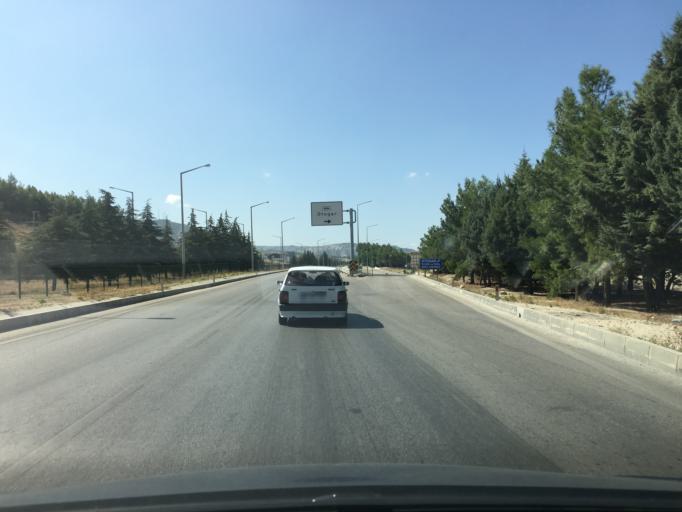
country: TR
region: Burdur
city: Burdur
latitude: 37.7392
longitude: 30.3119
